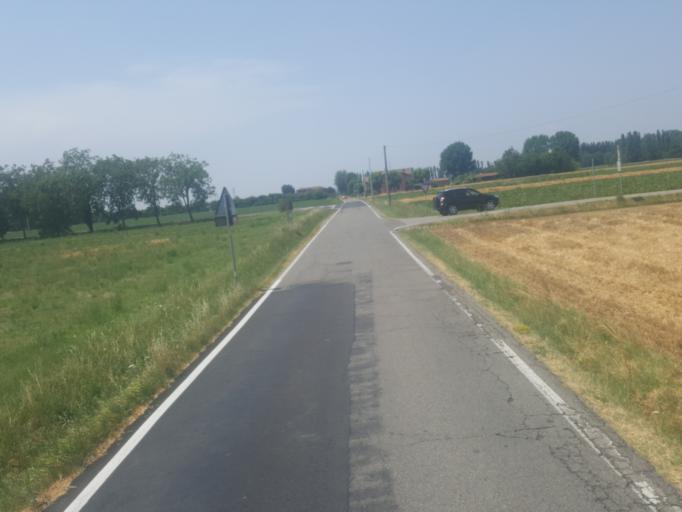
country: IT
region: Emilia-Romagna
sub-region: Provincia di Modena
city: Gaggio
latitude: 44.6239
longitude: 11.0419
